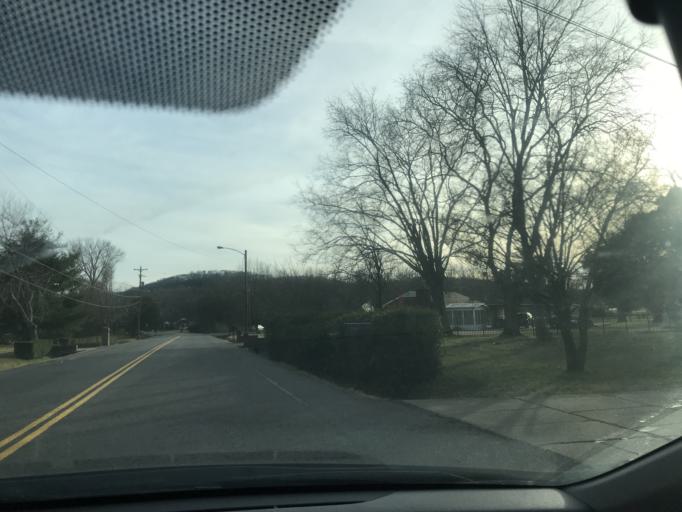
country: US
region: Tennessee
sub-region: Davidson County
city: Nashville
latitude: 36.2159
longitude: -86.8264
